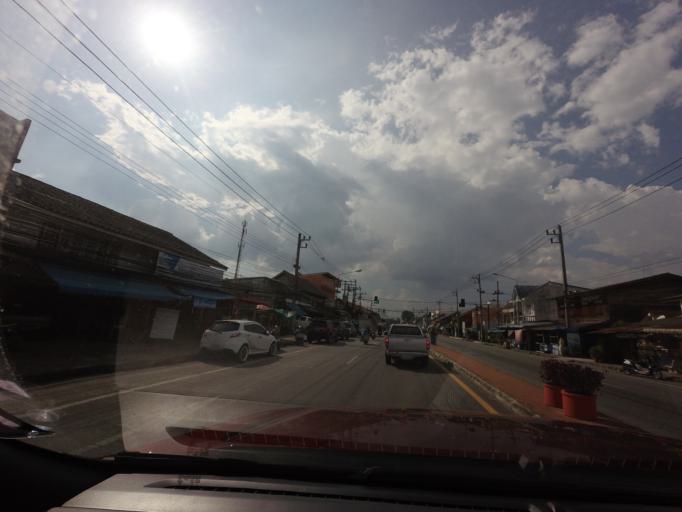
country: TH
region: Yala
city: Yala
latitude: 6.5786
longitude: 101.1985
